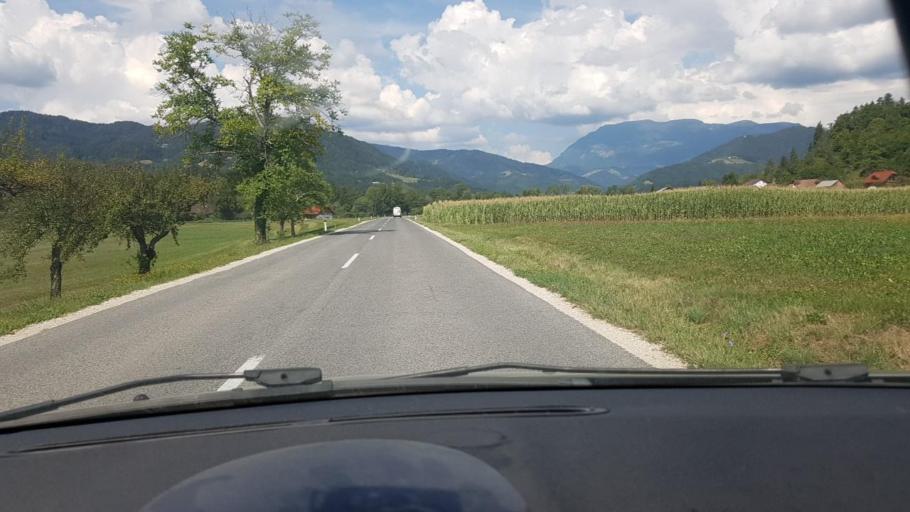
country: SI
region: Ljubno
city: Ljubno ob Savinji
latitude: 46.3256
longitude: 14.8658
